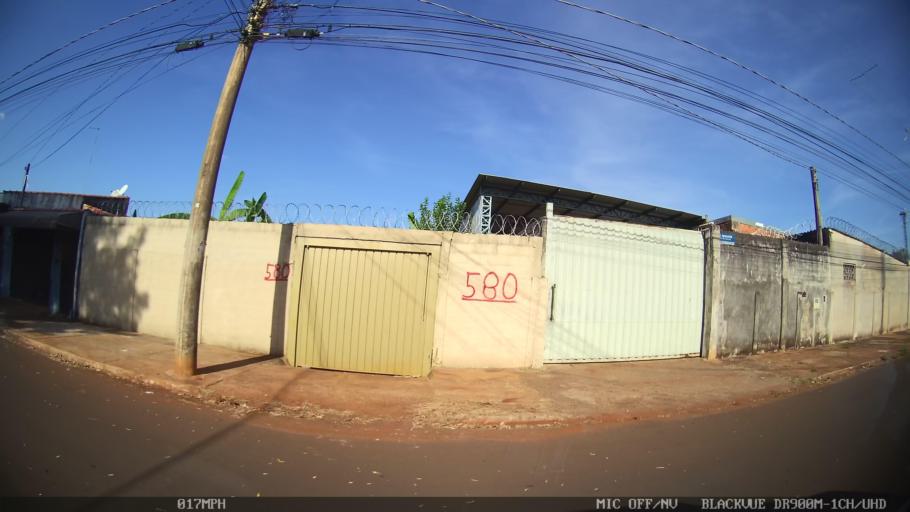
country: BR
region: Sao Paulo
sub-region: Ribeirao Preto
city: Ribeirao Preto
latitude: -21.1804
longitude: -47.7643
